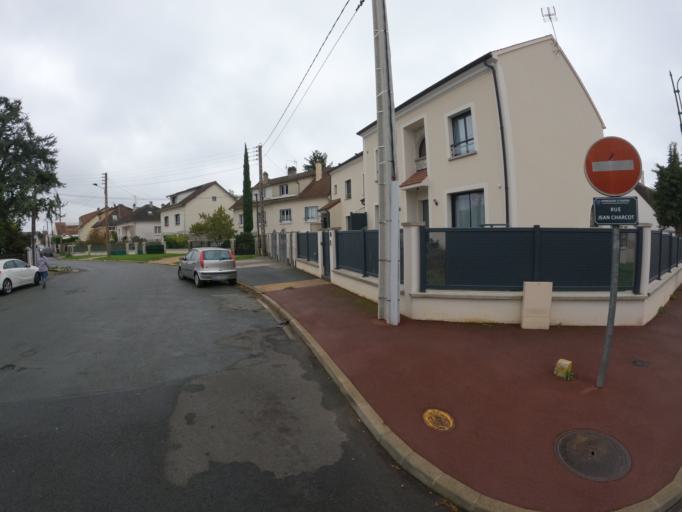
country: FR
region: Ile-de-France
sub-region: Departement du Val-de-Marne
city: Ormesson-sur-Marne
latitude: 48.7870
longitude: 2.5399
